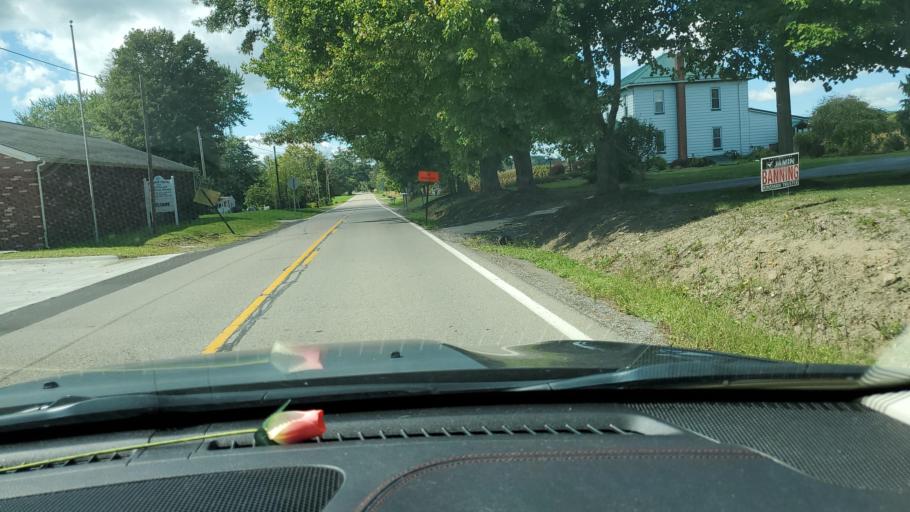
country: US
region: Ohio
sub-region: Ashtabula County
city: Andover
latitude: 41.4555
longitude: -80.5811
